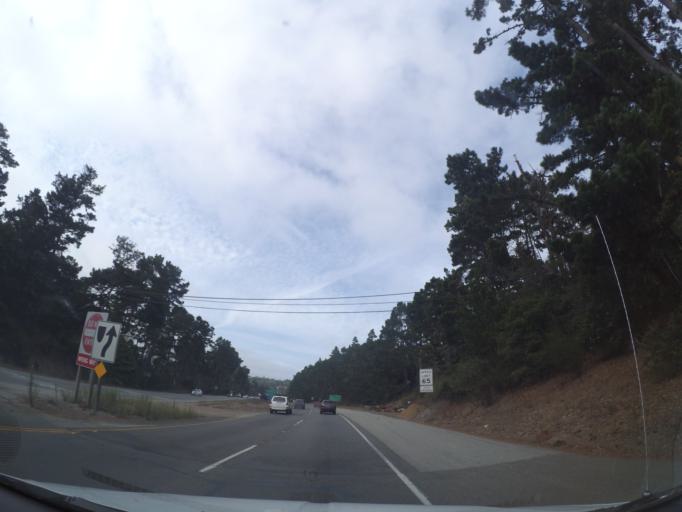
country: US
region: California
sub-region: Monterey County
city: Carmel-by-the-Sea
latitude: 36.5689
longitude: -121.9125
